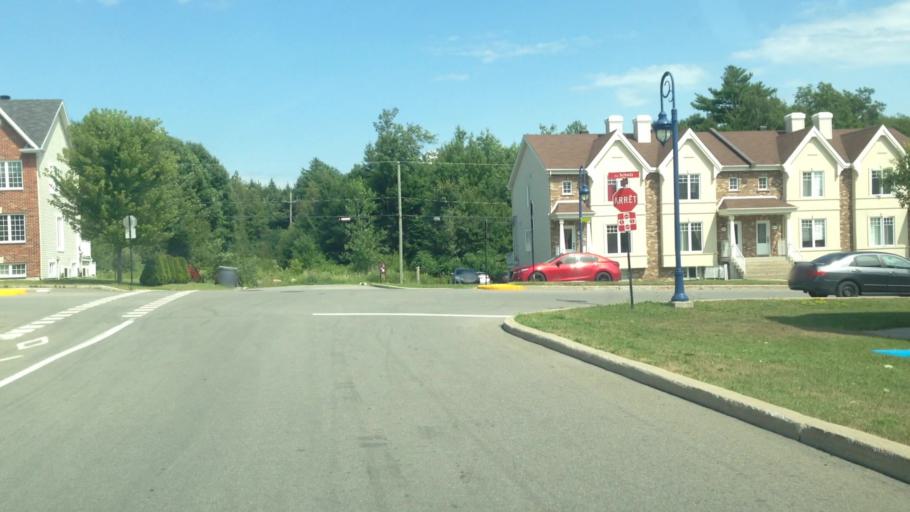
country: CA
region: Quebec
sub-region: Laurentides
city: Saint-Jerome
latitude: 45.8109
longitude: -73.9994
